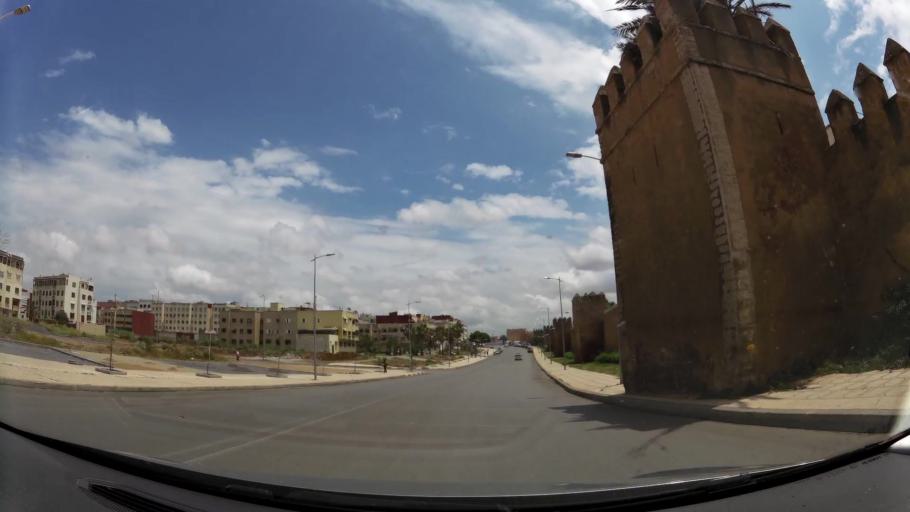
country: MA
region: Rabat-Sale-Zemmour-Zaer
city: Sale
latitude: 34.0434
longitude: -6.8235
